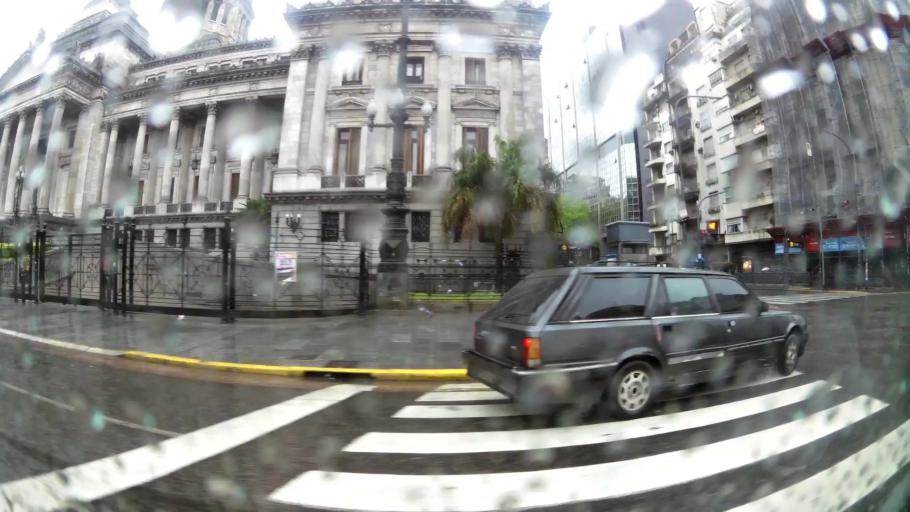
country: AR
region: Buenos Aires F.D.
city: Buenos Aires
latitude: -34.6094
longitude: -58.3920
